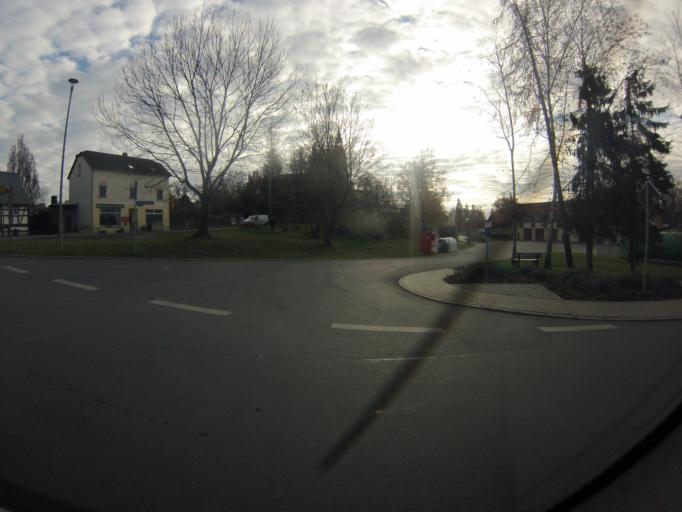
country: DE
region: Thuringia
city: Ponitz
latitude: 50.8580
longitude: 12.4244
